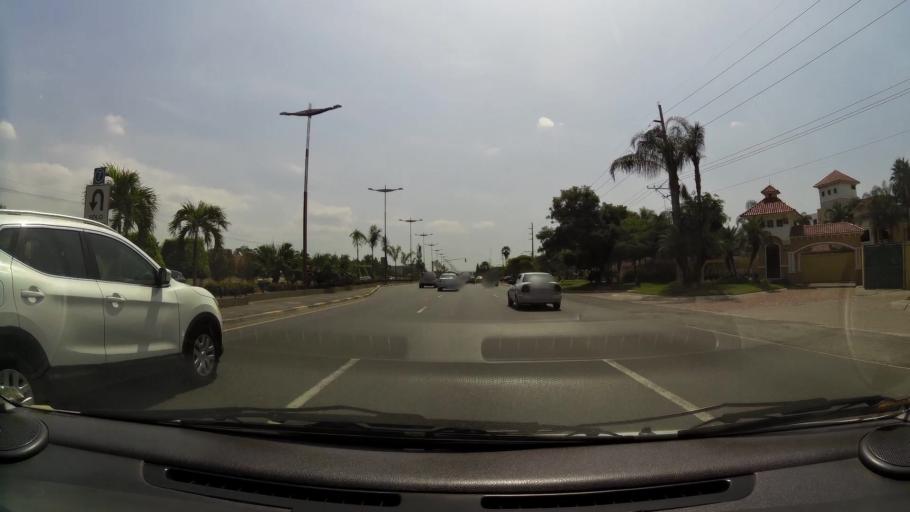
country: EC
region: Guayas
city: Eloy Alfaro
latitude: -2.1177
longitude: -79.8678
